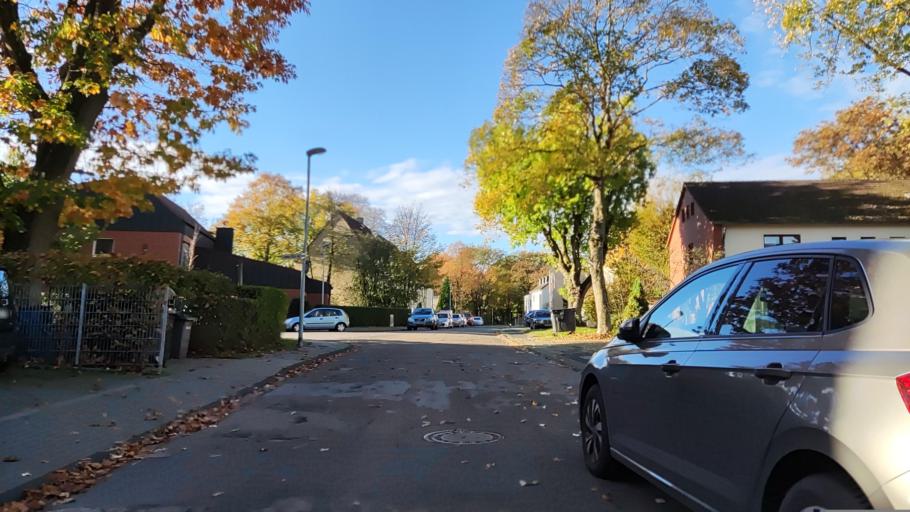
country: DE
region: North Rhine-Westphalia
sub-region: Regierungsbezirk Arnsberg
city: Herne
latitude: 51.5313
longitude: 7.1967
